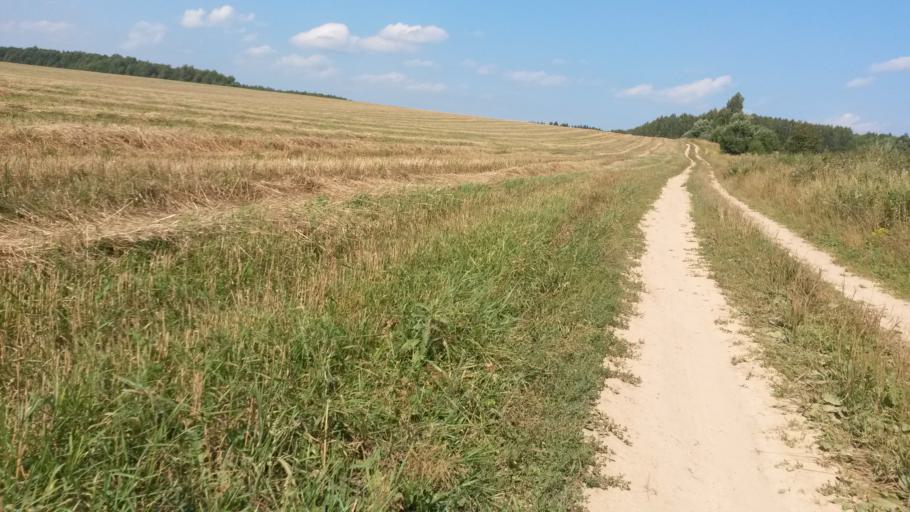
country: RU
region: Jaroslavl
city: Gavrilov-Yam
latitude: 57.3107
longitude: 39.9654
